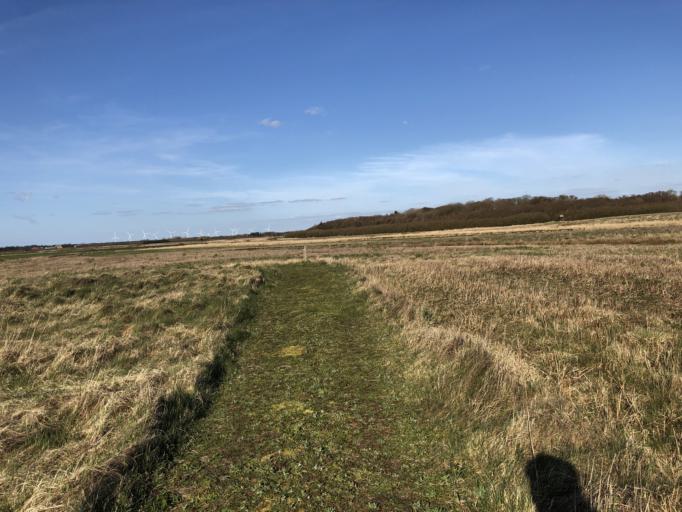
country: DK
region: Central Jutland
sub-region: Holstebro Kommune
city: Ulfborg
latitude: 56.3240
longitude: 8.3222
